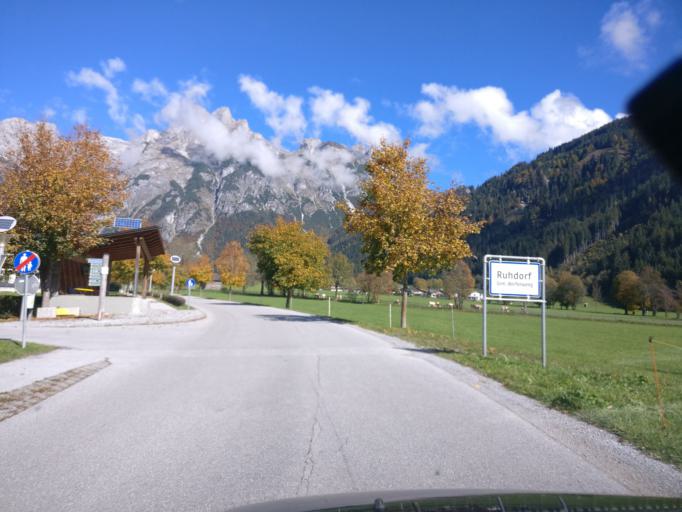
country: AT
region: Salzburg
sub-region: Politischer Bezirk Sankt Johann im Pongau
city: Werfenweng
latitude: 47.4656
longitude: 13.2630
